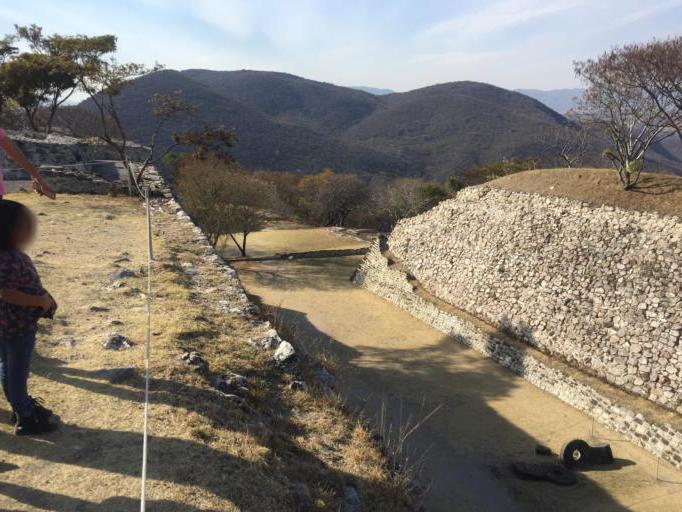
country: MX
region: Morelos
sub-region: Miacatlan
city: Xochicalco (Cirenio Longares)
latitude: 18.8054
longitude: -99.2963
